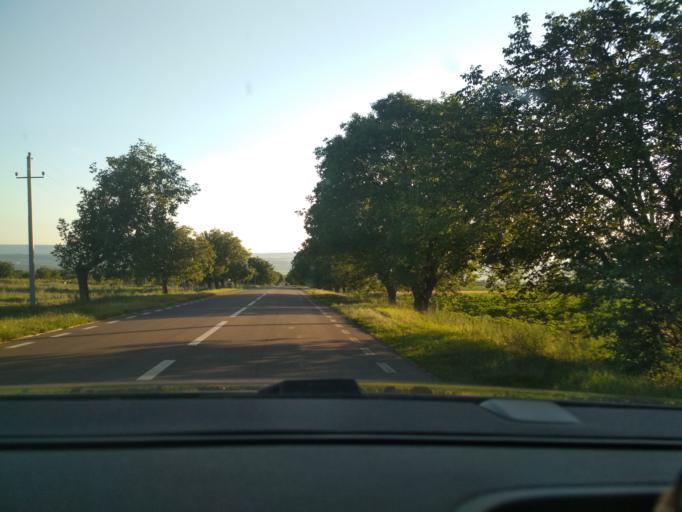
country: RO
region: Iasi
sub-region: Comuna Gorban
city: Gorban
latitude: 46.9487
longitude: 28.1518
